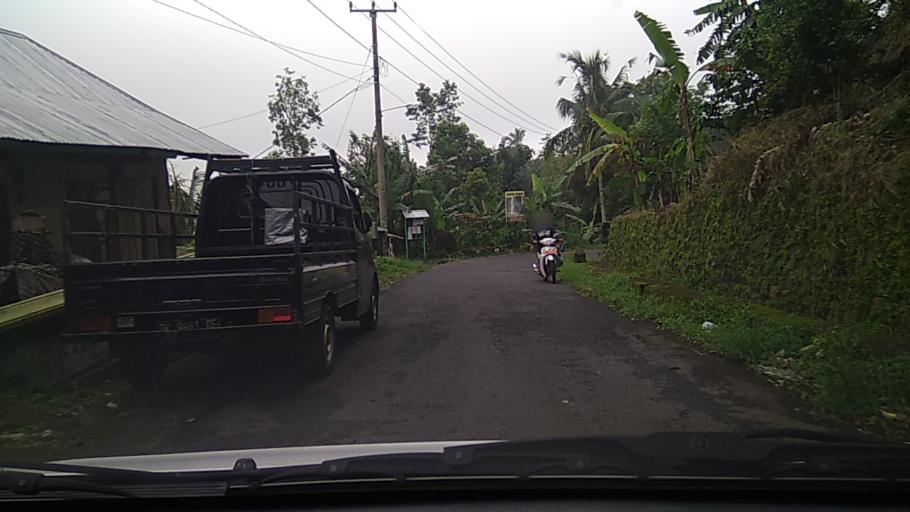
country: ID
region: Bali
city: Banjar Padangbulia
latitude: -8.1744
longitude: 115.1876
